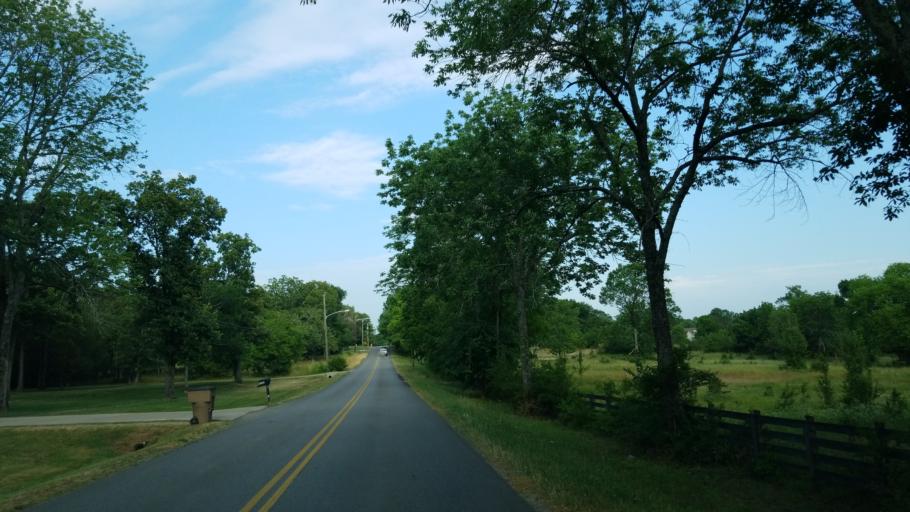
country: US
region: Tennessee
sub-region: Rutherford County
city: La Vergne
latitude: 36.0379
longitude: -86.5910
